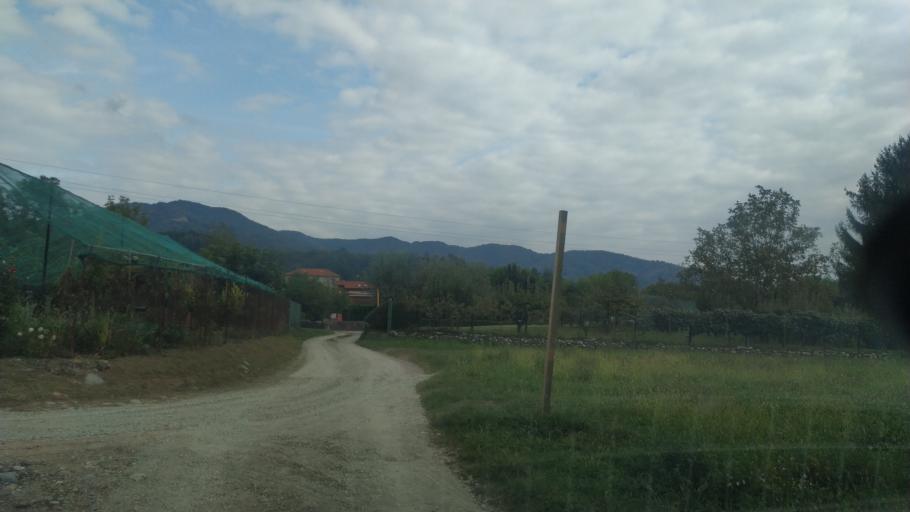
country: IT
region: Piedmont
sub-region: Provincia di Novara
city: Grignasco
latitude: 45.6784
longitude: 8.3359
